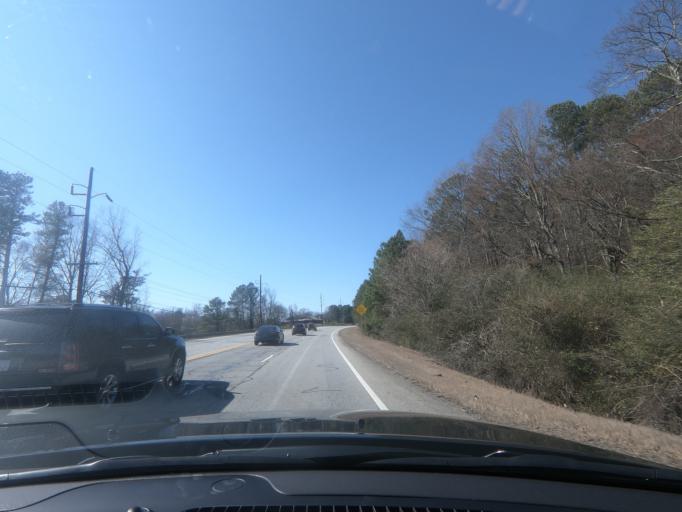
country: US
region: Georgia
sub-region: Gordon County
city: Calhoun
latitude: 34.4735
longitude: -84.9672
